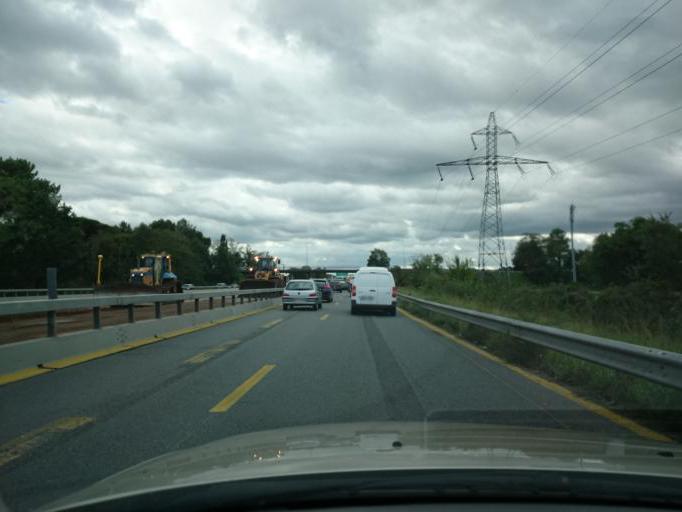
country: FR
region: Aquitaine
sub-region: Departement de la Gironde
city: Pessac
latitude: 44.8292
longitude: -0.6759
